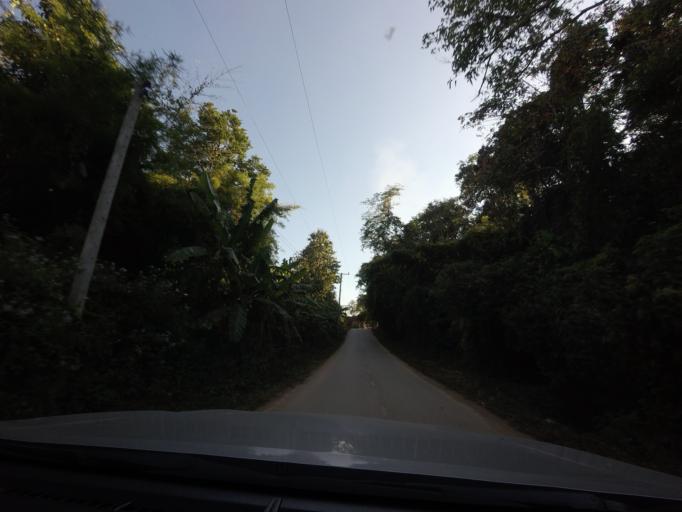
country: TH
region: Lampang
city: Chae Hom
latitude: 18.5962
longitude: 99.6269
